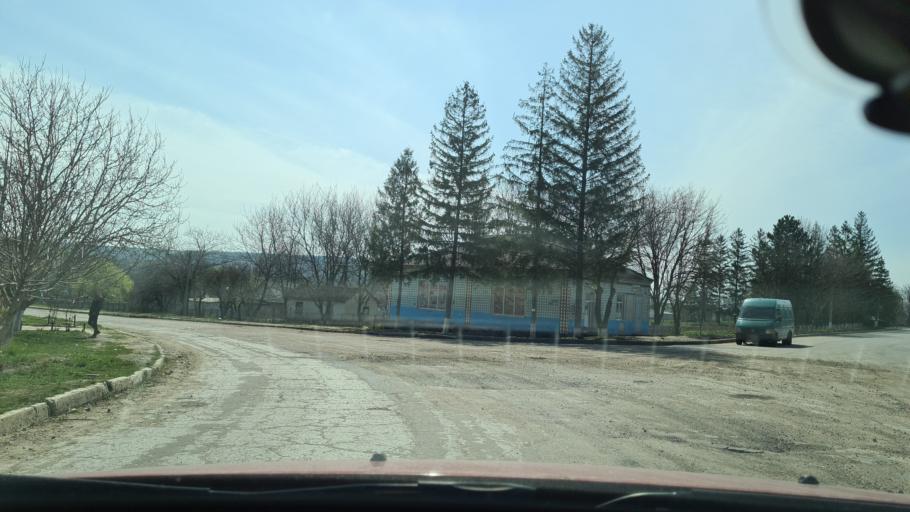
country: MD
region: Ungheni
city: Ungheni
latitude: 47.2693
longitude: 27.9304
